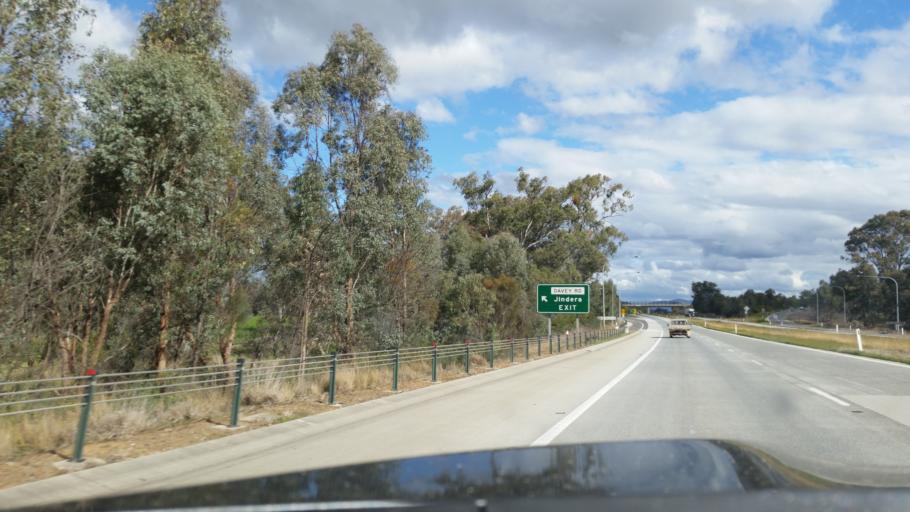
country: AU
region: New South Wales
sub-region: Albury Municipality
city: Lavington
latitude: -35.9963
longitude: 146.9933
